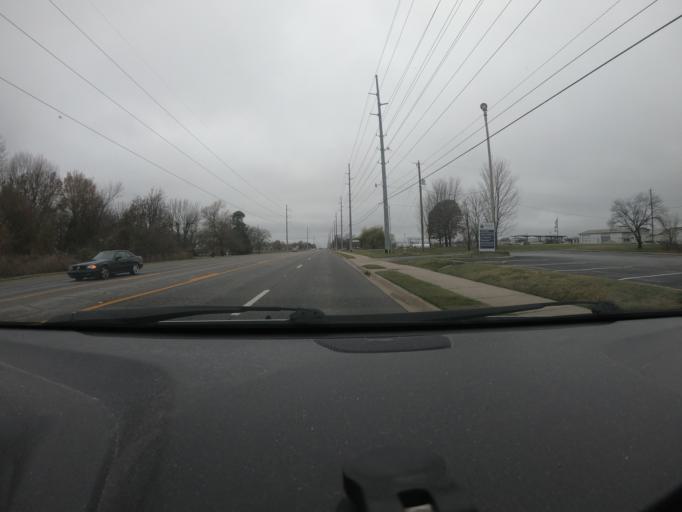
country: US
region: Arkansas
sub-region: Benton County
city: Bentonville
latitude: 36.3574
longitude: -94.2255
